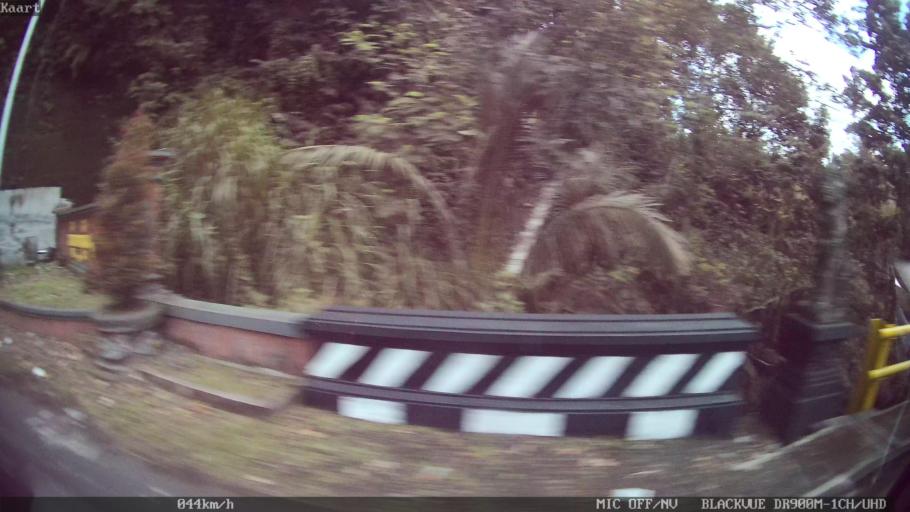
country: ID
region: Bali
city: Banjar Kubu
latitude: -8.4070
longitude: 115.4273
